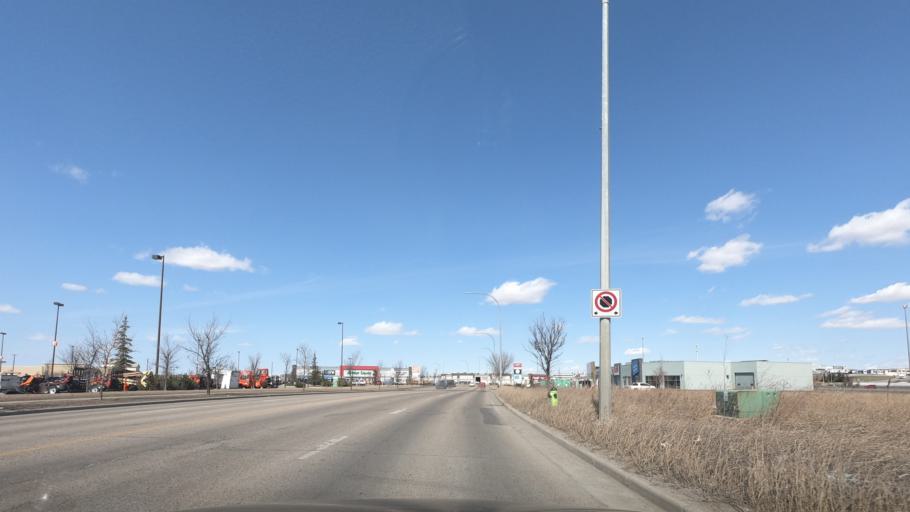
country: CA
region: Alberta
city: Airdrie
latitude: 51.2596
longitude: -114.0048
